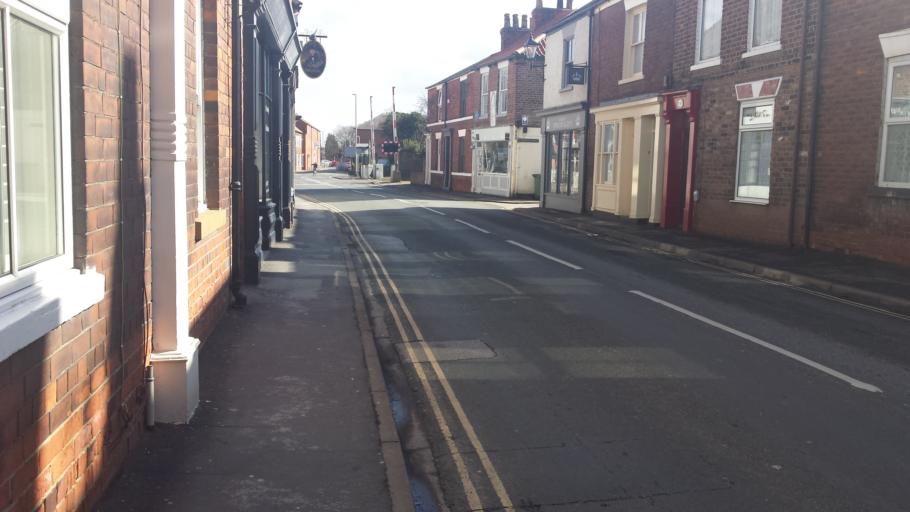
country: GB
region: England
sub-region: East Riding of Yorkshire
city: Beverley
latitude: 53.8392
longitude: -0.4232
